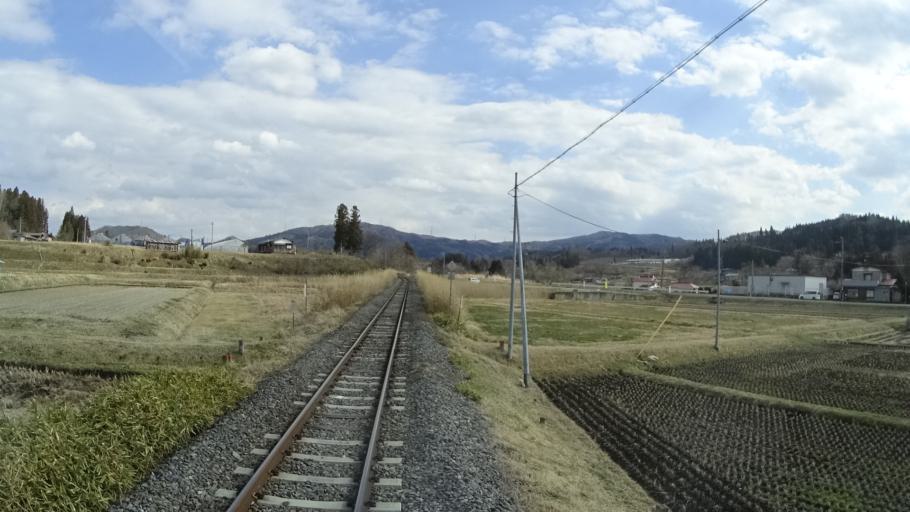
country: JP
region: Iwate
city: Hanamaki
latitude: 39.3641
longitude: 141.2607
